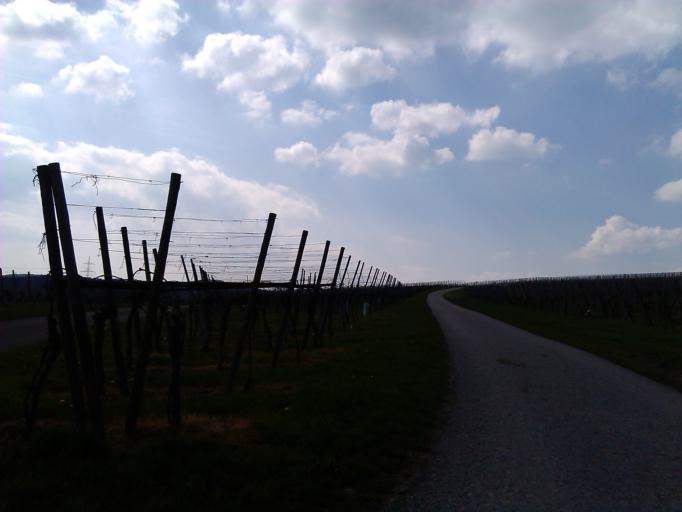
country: DE
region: Baden-Wuerttemberg
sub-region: Regierungsbezirk Stuttgart
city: Gemmingen
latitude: 49.1337
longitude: 8.9907
